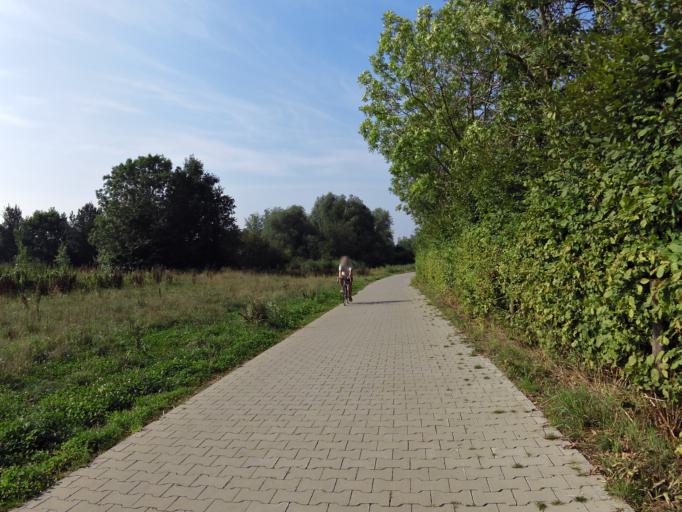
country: DE
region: North Rhine-Westphalia
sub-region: Regierungsbezirk Koln
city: Ubach-Palenberg
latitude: 50.9341
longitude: 6.0979
